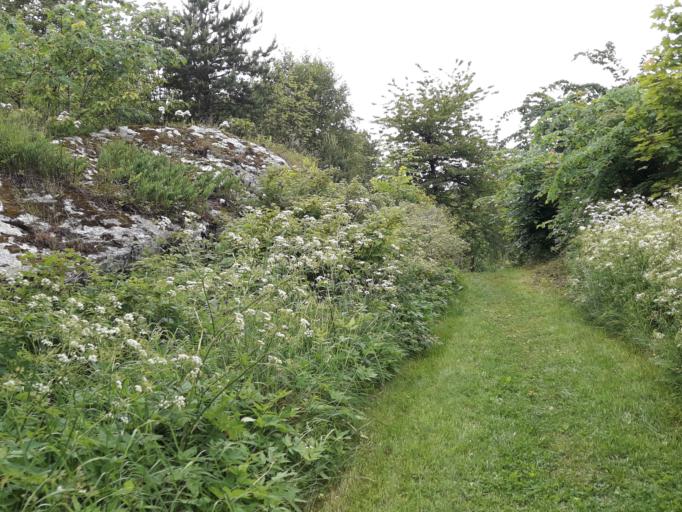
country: NO
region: Akershus
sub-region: Frogn
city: Drobak
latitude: 59.6751
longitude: 10.6073
